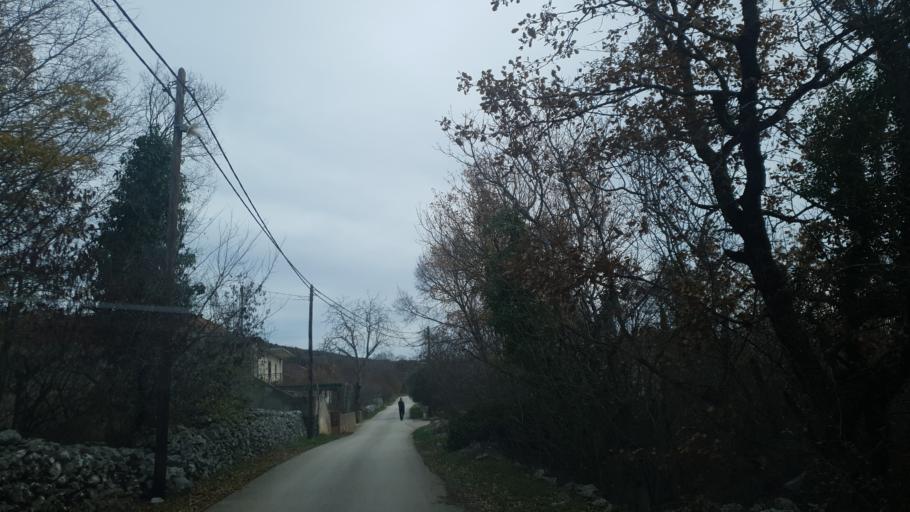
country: HR
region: Splitsko-Dalmatinska
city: Imotski
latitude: 43.4460
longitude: 17.2404
